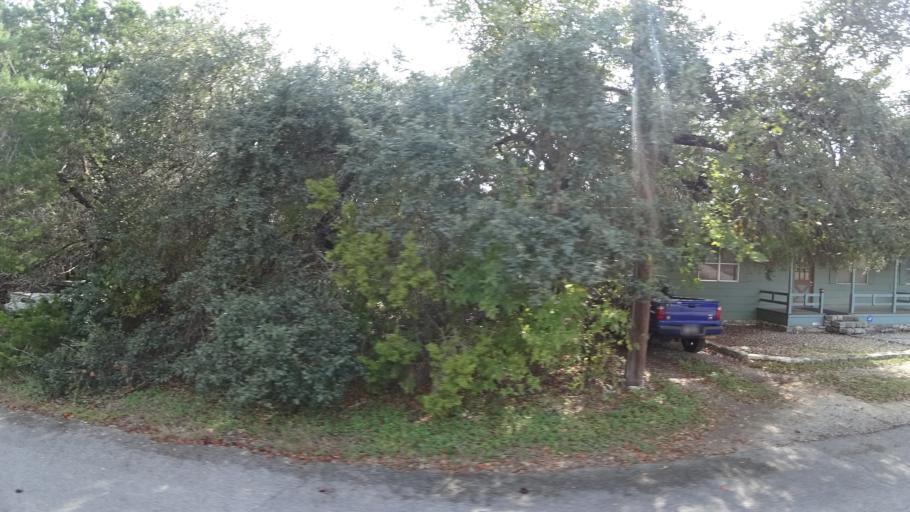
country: US
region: Texas
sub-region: Travis County
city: Hudson Bend
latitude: 30.3832
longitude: -97.9275
